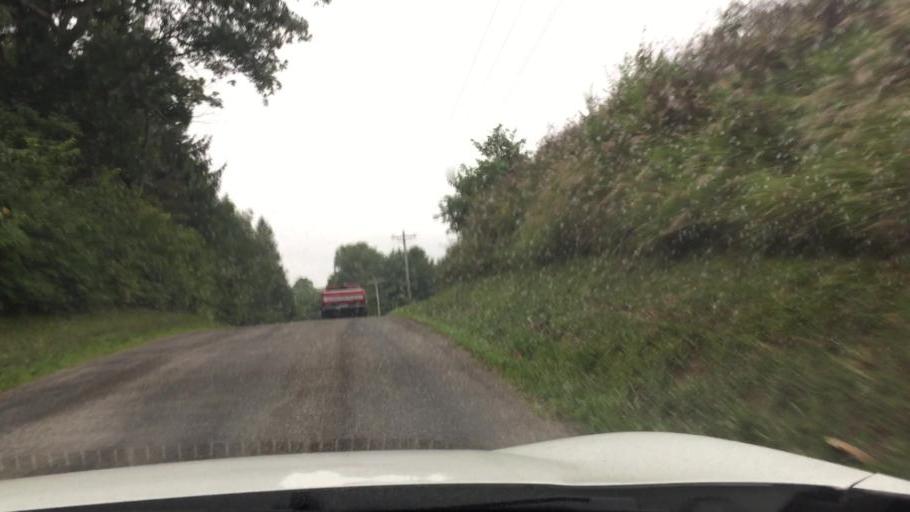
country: US
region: Ohio
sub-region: Champaign County
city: Mechanicsburg
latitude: 40.0380
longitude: -83.5955
